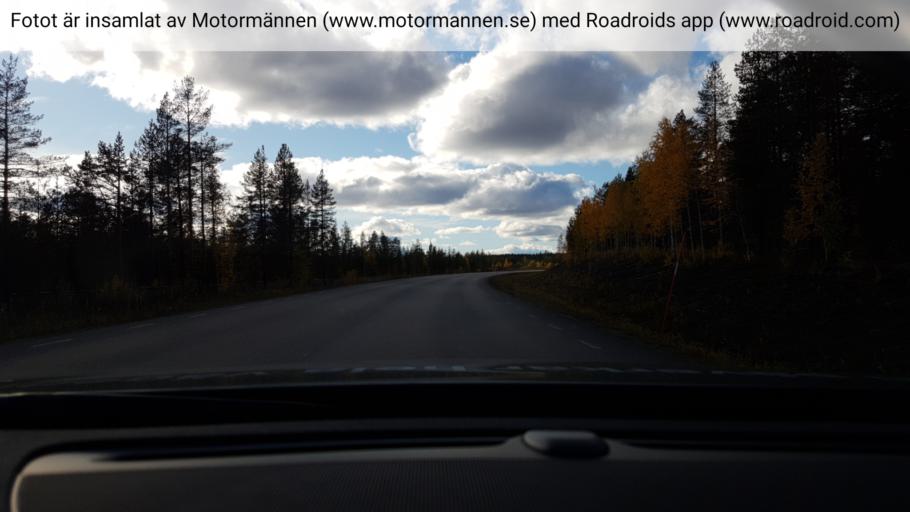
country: SE
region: Norrbotten
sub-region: Gallivare Kommun
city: Malmberget
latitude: 67.1634
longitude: 20.7104
